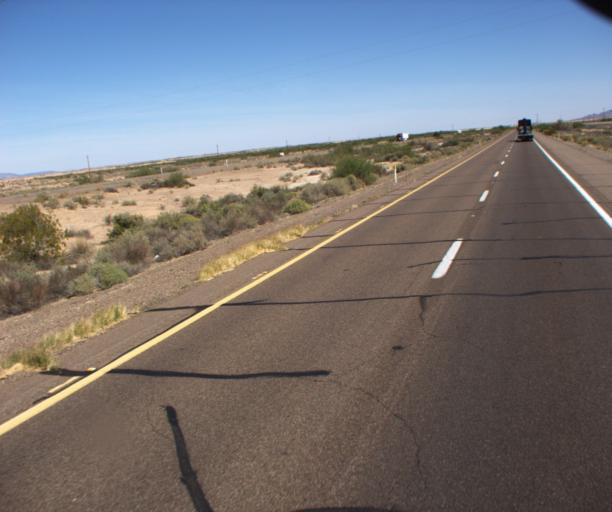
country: US
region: Arizona
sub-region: Yuma County
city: Wellton
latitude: 32.7482
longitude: -113.6675
